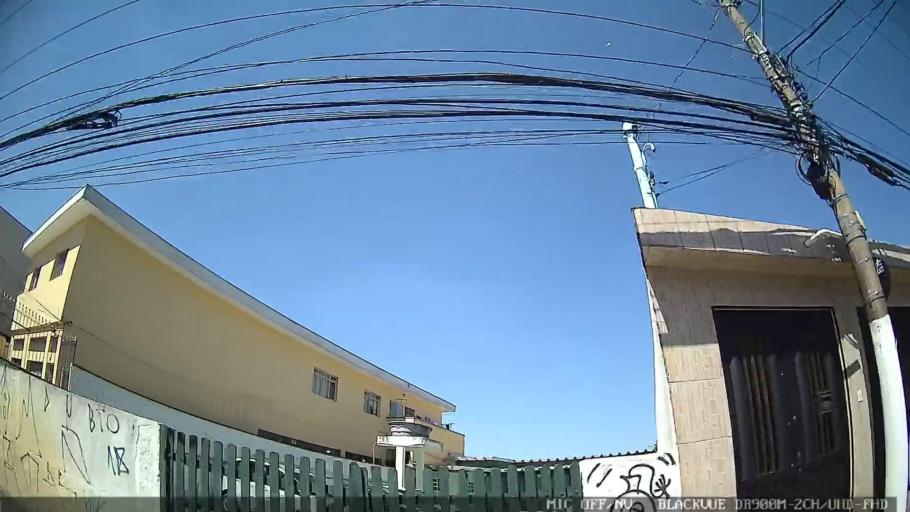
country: BR
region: Sao Paulo
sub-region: Sao Caetano Do Sul
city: Sao Caetano do Sul
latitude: -23.5935
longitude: -46.5195
